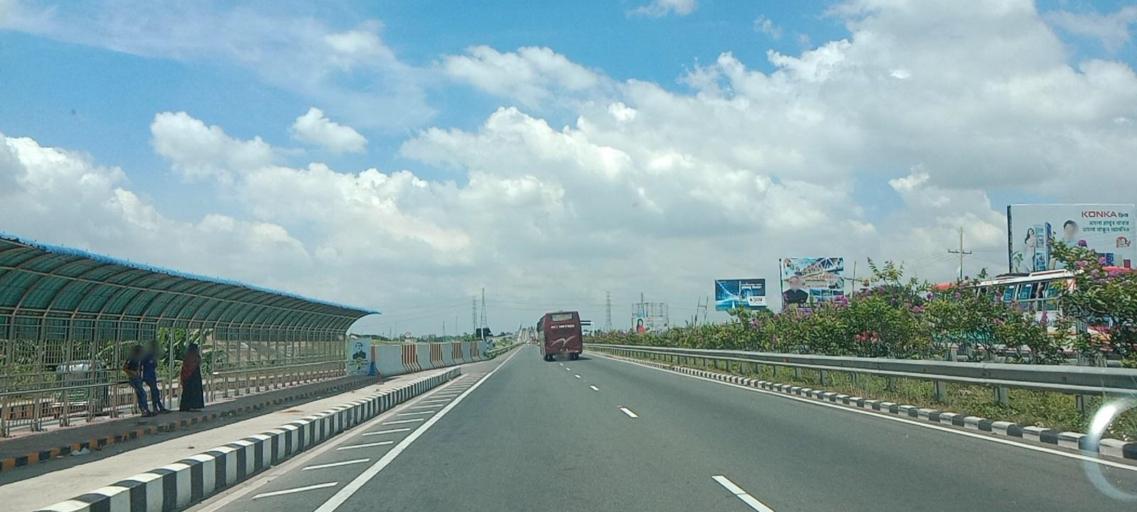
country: BD
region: Dhaka
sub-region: Dhaka
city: Dhaka
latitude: 23.6177
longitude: 90.3337
